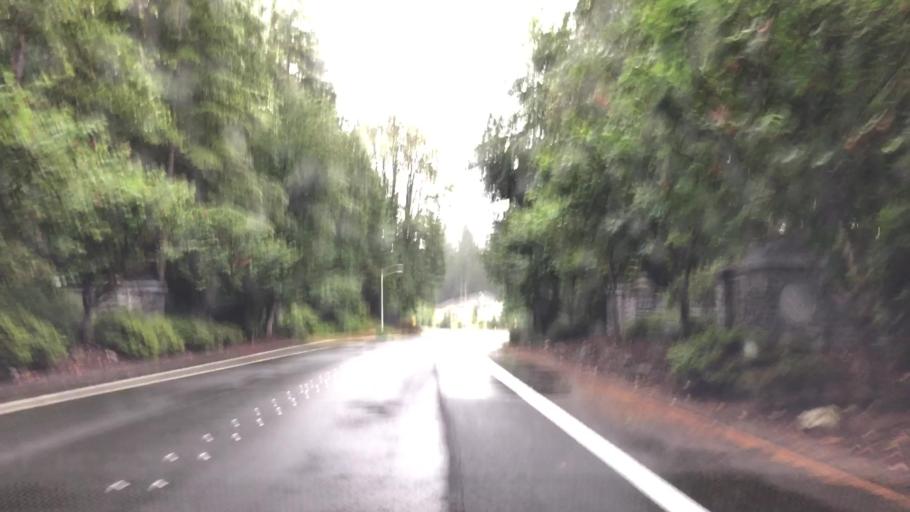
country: US
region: Washington
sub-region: Snohomish County
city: Maltby
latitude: 47.7865
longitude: -122.1276
